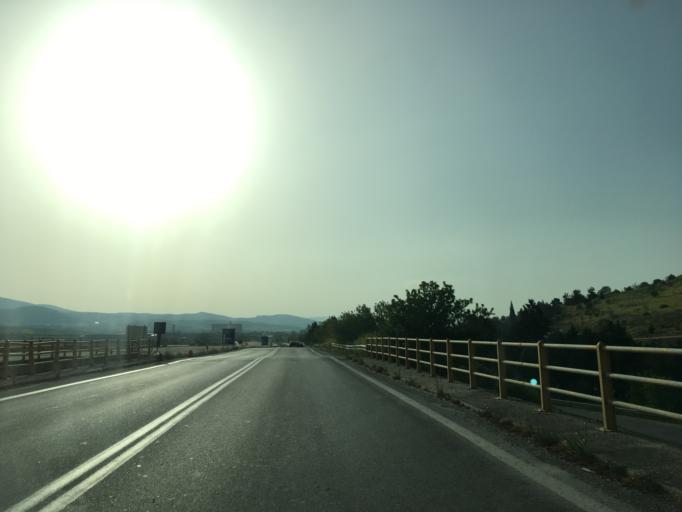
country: GR
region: Thessaly
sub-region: Nomos Magnisias
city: Velestino
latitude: 39.3864
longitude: 22.7899
